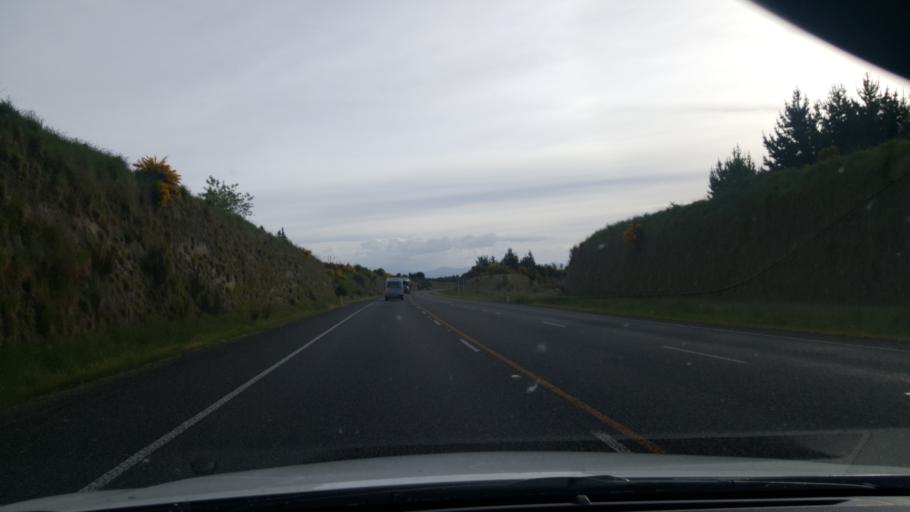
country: NZ
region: Waikato
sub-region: Taupo District
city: Taupo
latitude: -38.7208
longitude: 176.1008
